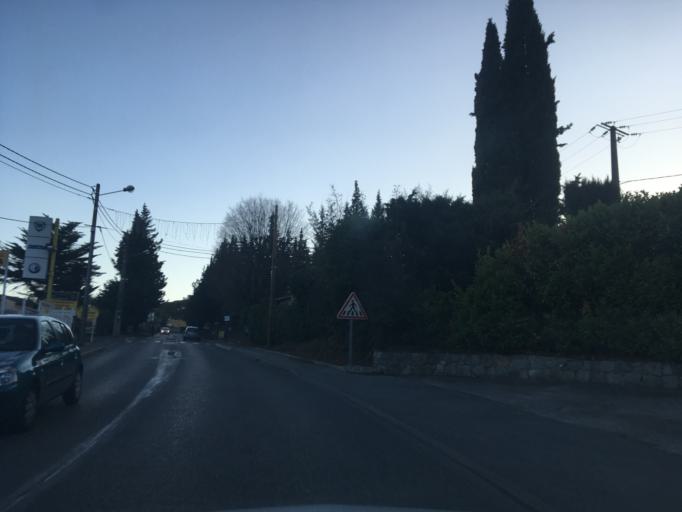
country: FR
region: Provence-Alpes-Cote d'Azur
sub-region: Departement des Alpes-Maritimes
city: Peymeinade
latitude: 43.6382
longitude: 6.8649
